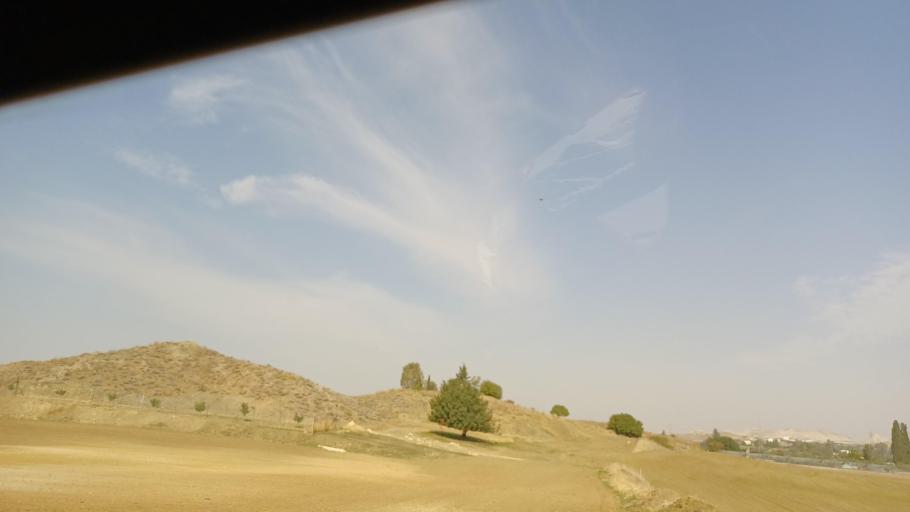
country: CY
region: Larnaka
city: Mosfiloti
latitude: 34.9662
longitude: 33.4385
